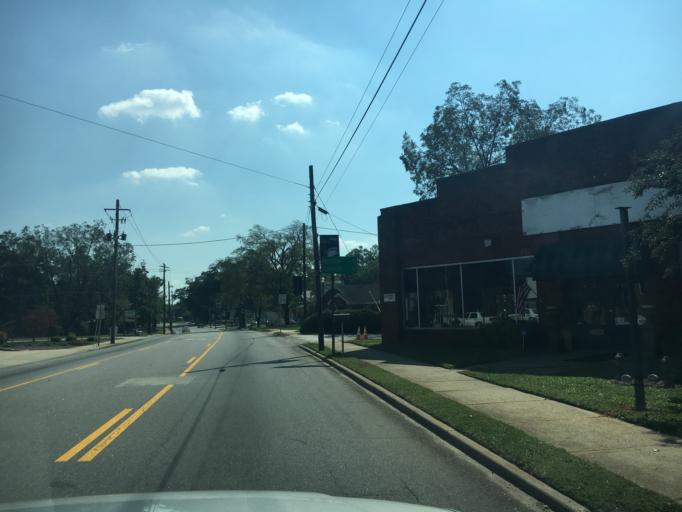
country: US
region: Georgia
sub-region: Franklin County
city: Lavonia
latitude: 34.4353
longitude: -83.1074
